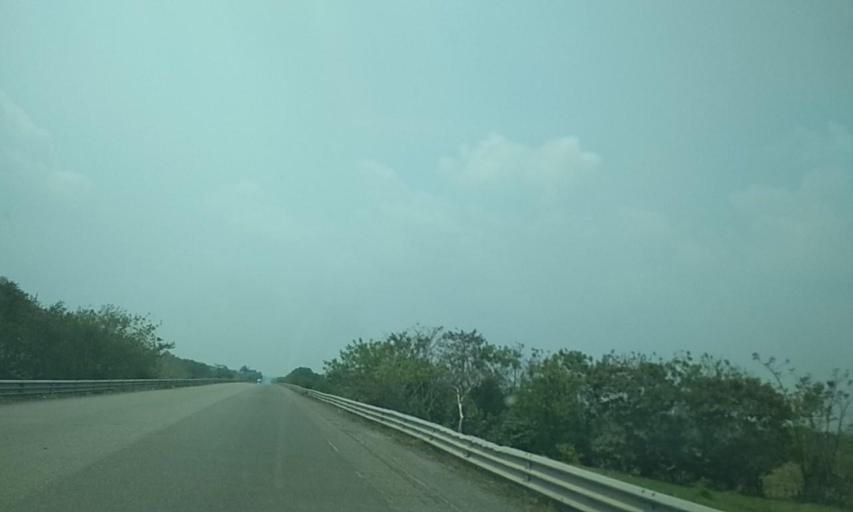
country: MX
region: Tabasco
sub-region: Huimanguillo
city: Francisco Rueda
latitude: 17.7759
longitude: -94.0480
